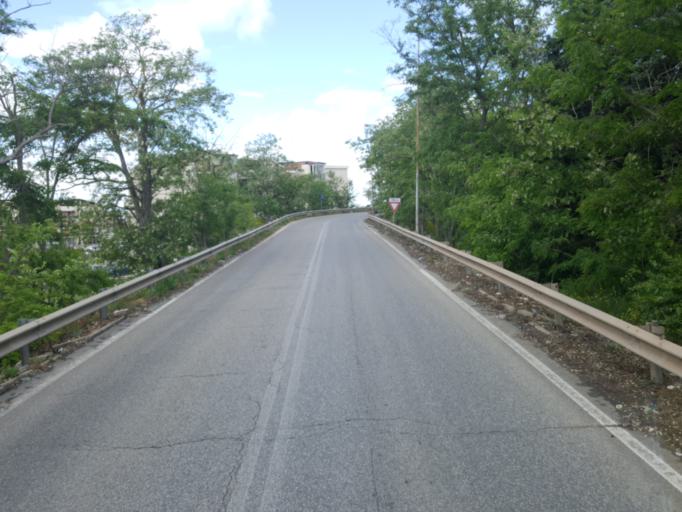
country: IT
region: Apulia
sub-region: Provincia di Bari
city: Altamura
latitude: 40.8141
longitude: 16.5535
